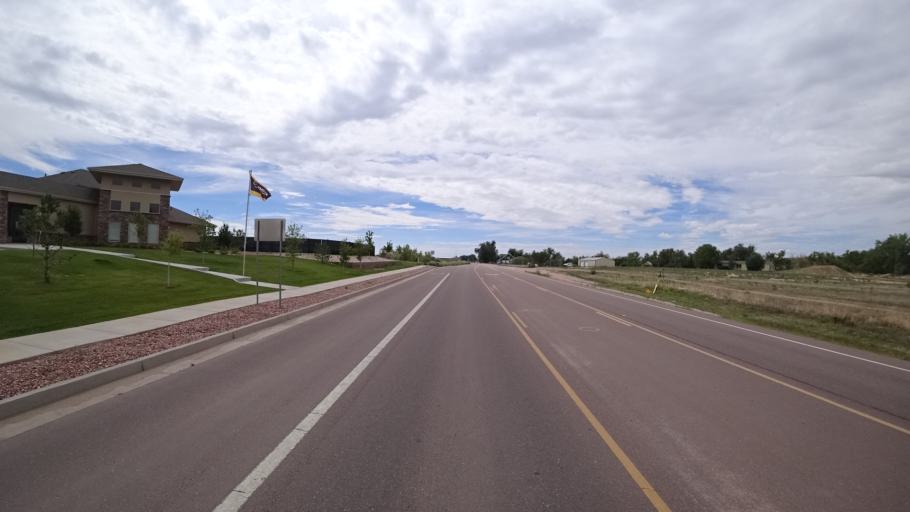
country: US
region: Colorado
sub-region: El Paso County
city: Fountain
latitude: 38.6714
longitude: -104.6955
